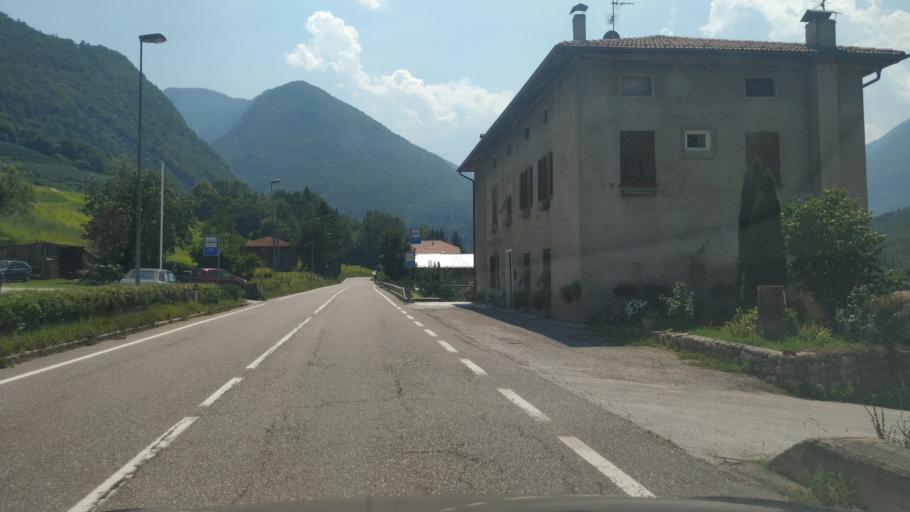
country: IT
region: Trentino-Alto Adige
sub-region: Provincia di Trento
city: Denno
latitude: 46.2471
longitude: 11.0624
